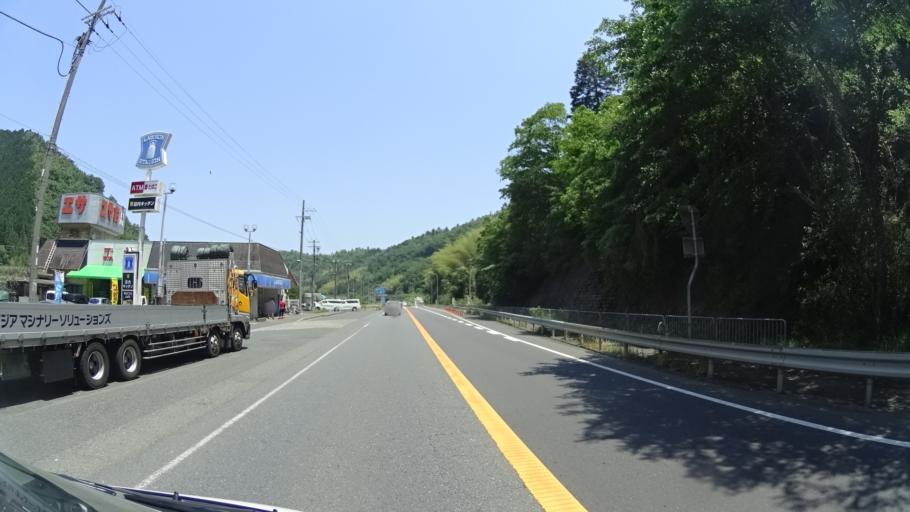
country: JP
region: Kyoto
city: Maizuru
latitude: 35.4105
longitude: 135.3295
